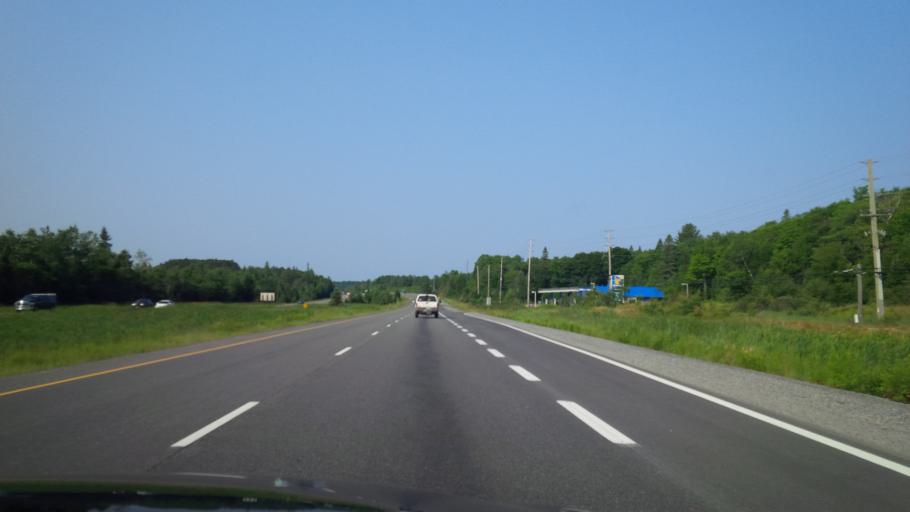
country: CA
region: Ontario
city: Huntsville
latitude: 45.3011
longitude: -79.2537
